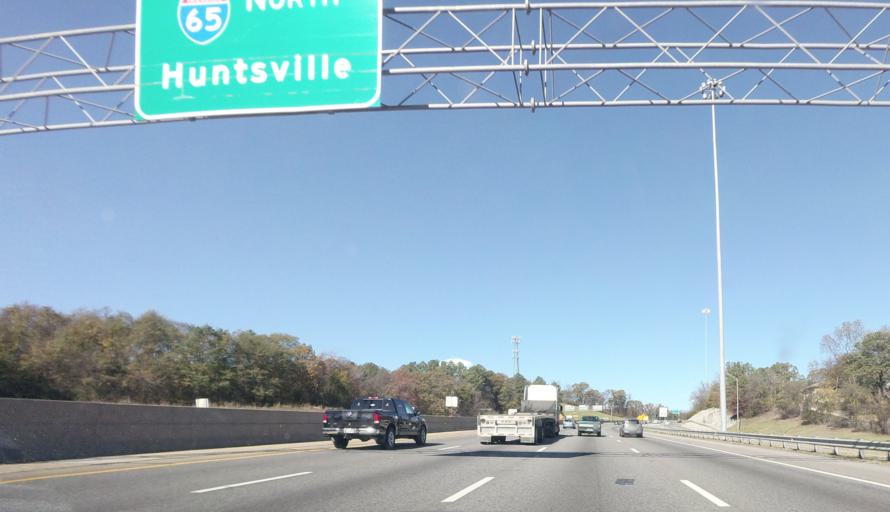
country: US
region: Alabama
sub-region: Jefferson County
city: Birmingham
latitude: 33.5530
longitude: -86.8305
